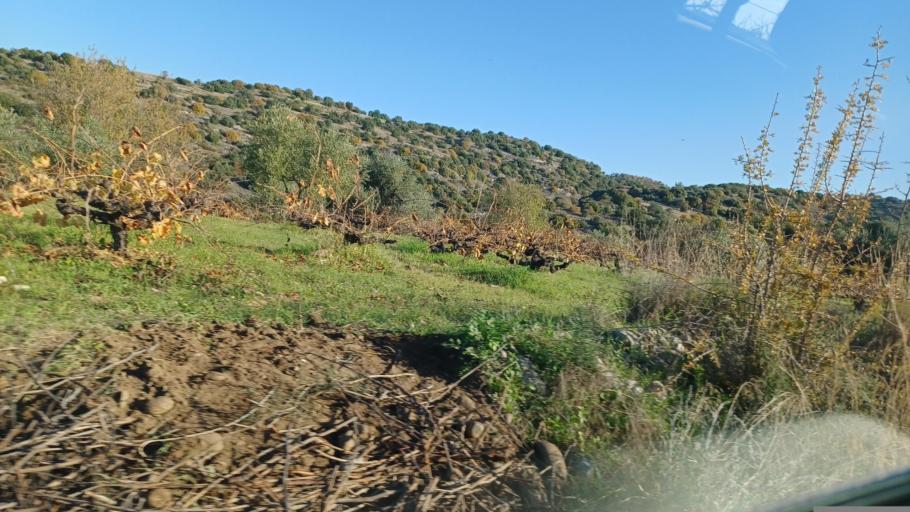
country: CY
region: Pafos
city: Mesogi
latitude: 34.8688
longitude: 32.5684
